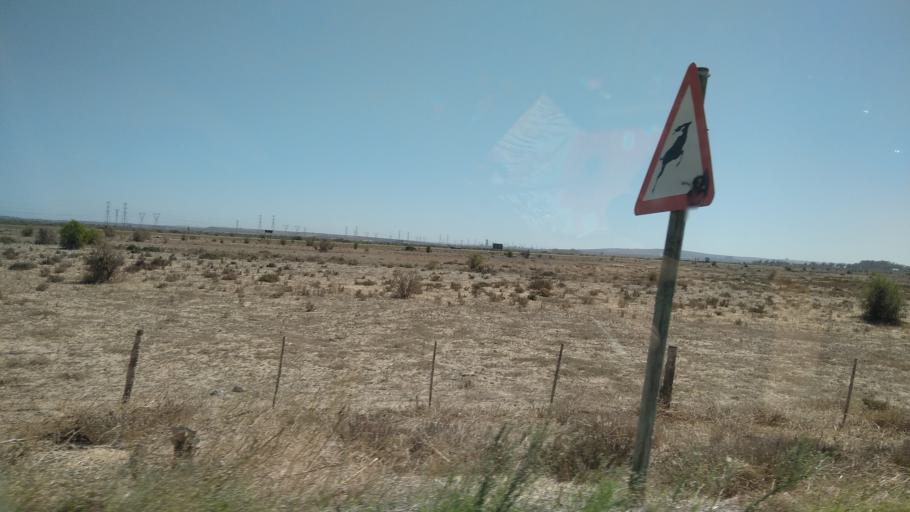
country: ZA
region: Western Cape
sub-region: West Coast District Municipality
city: Saldanha
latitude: -33.0232
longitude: 18.1084
